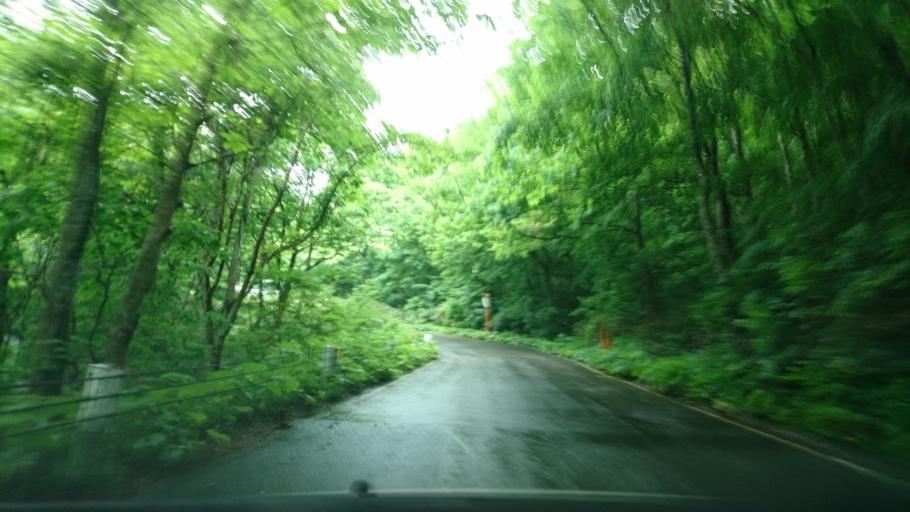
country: JP
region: Iwate
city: Ichinoseki
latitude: 38.9953
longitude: 140.8314
